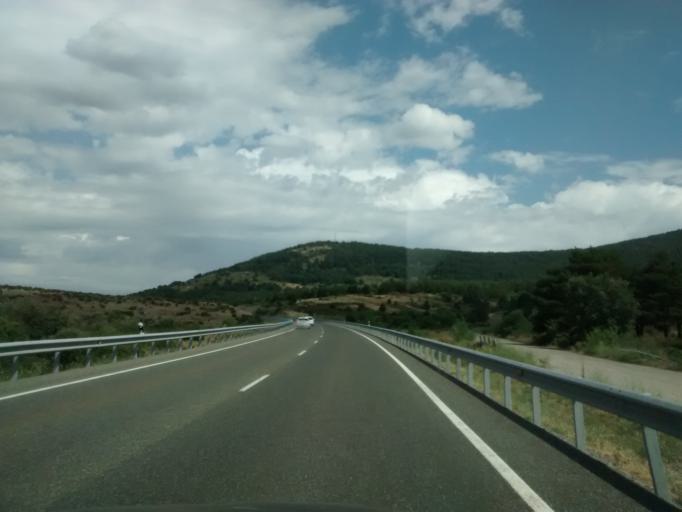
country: ES
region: Castille and Leon
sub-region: Provincia de Segovia
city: Torre Val de San Pedro
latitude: 41.0610
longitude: -3.8803
